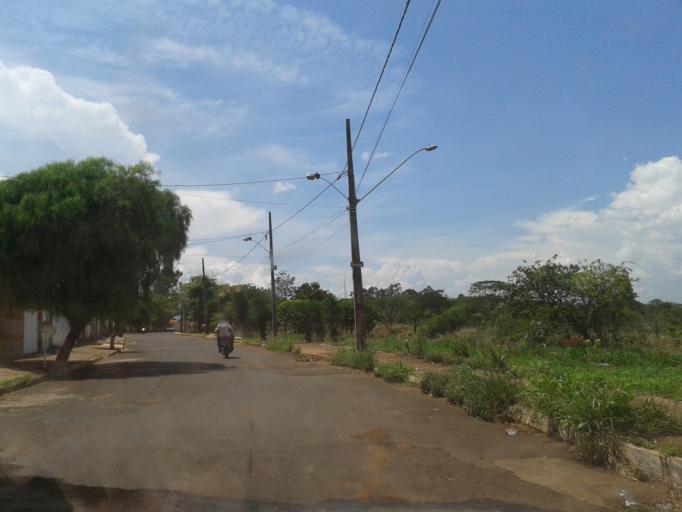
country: BR
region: Minas Gerais
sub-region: Araguari
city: Araguari
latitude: -18.6742
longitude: -48.1842
